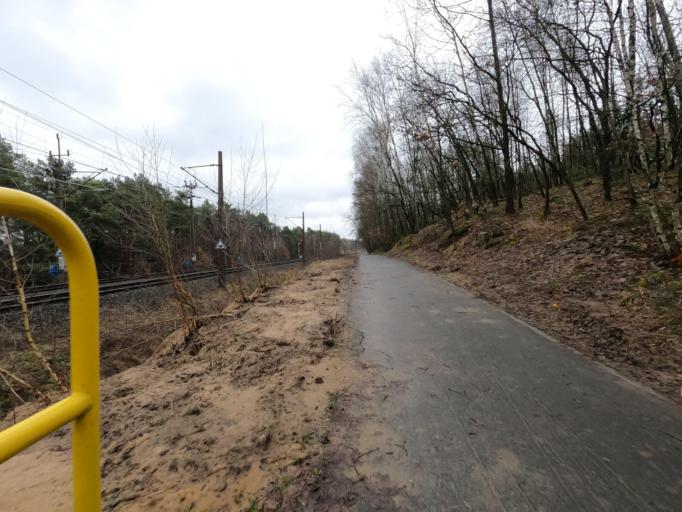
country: PL
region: Greater Poland Voivodeship
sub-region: Powiat pilski
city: Kaczory
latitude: 53.1086
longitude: 16.8712
